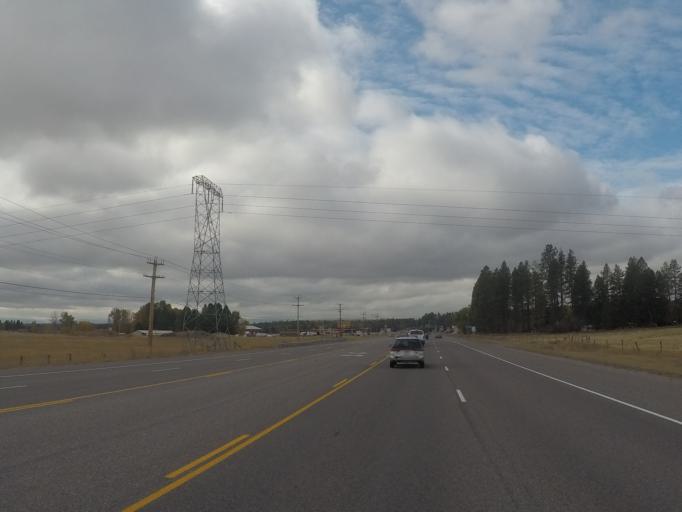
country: US
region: Montana
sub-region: Flathead County
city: Columbia Falls
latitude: 48.3708
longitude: -114.2321
